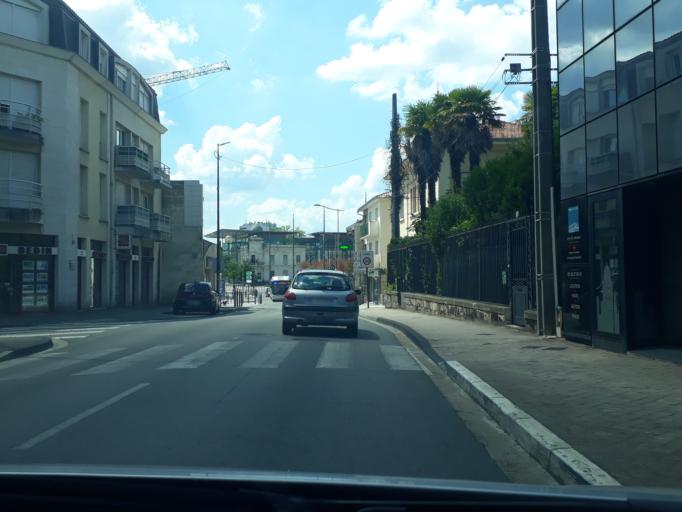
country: FR
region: Aquitaine
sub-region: Departement de la Gironde
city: Merignac
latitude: 44.8415
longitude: -0.6455
